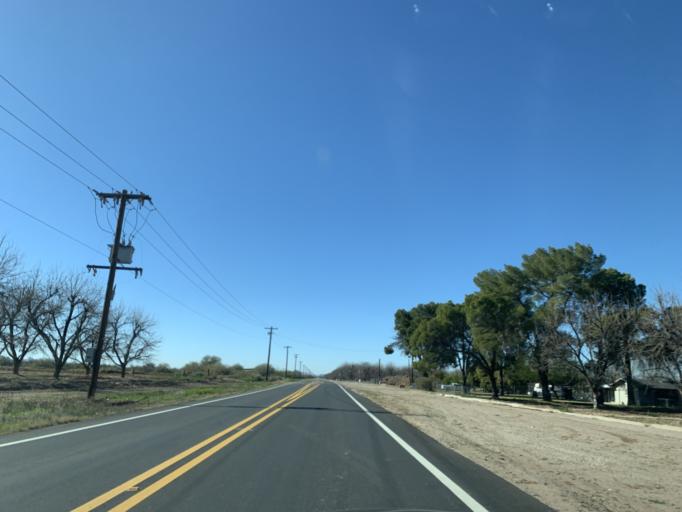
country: US
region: Arizona
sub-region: Pinal County
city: Eloy
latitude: 32.7197
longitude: -111.5147
